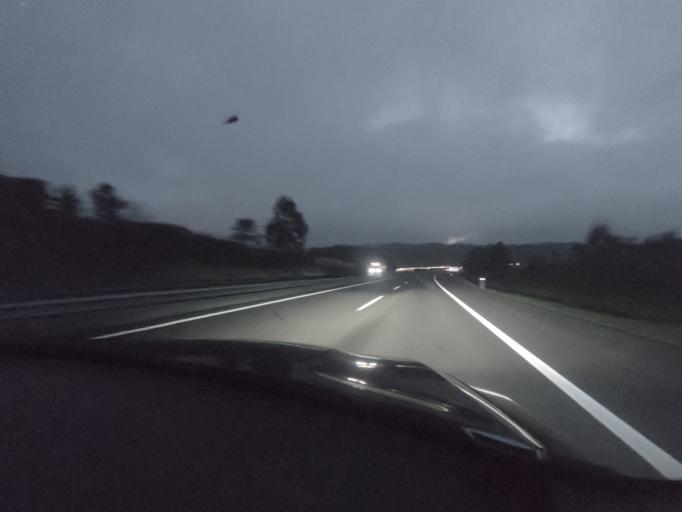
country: PT
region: Leiria
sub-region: Leiria
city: Caranguejeira
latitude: 39.8100
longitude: -8.7225
